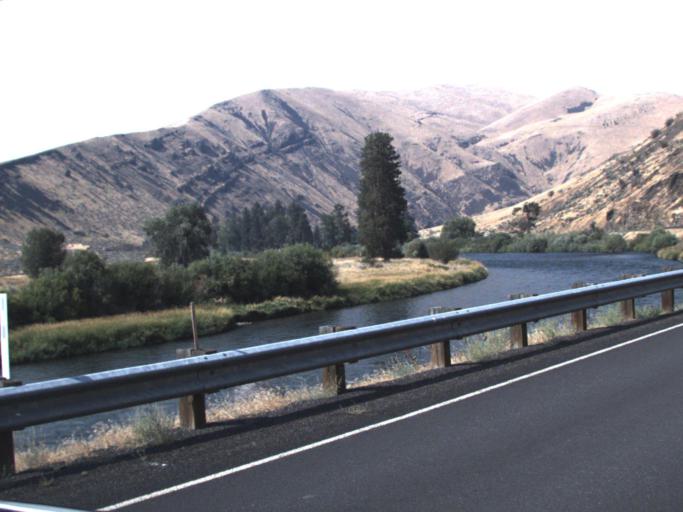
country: US
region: Washington
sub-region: Yakima County
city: Selah
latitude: 46.7882
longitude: -120.4504
